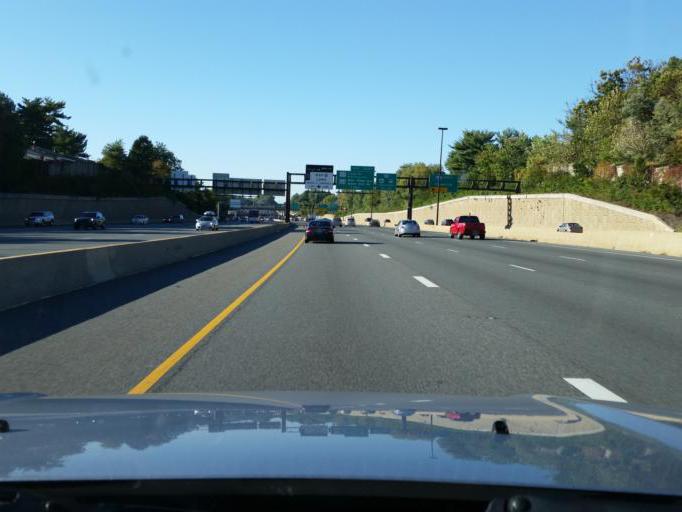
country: US
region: Maryland
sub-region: Montgomery County
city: Gaithersburg
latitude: 39.1258
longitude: -77.2013
